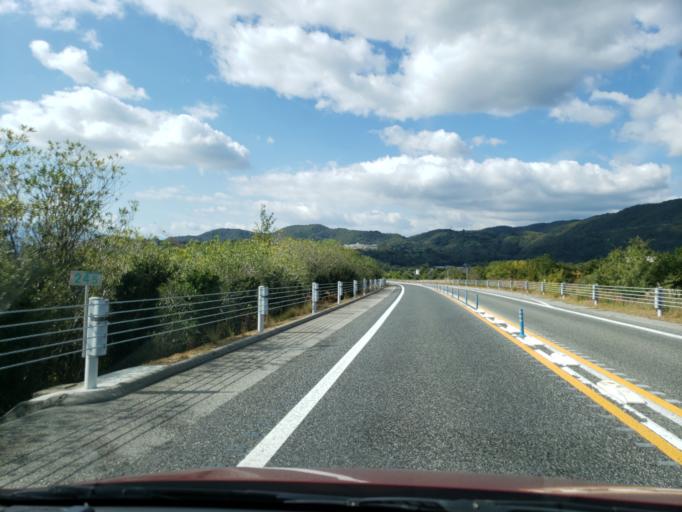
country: JP
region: Tokushima
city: Kamojimacho-jogejima
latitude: 34.1186
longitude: 134.3334
